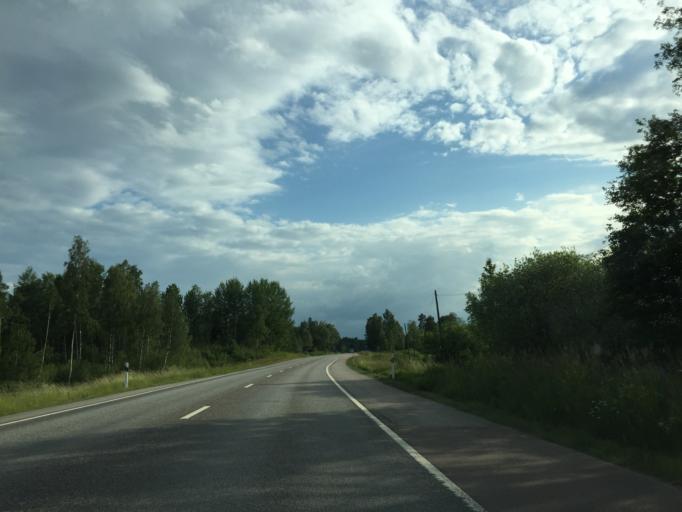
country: SE
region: OErebro
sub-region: Lindesbergs Kommun
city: Fellingsbro
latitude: 59.3630
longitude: 15.6937
